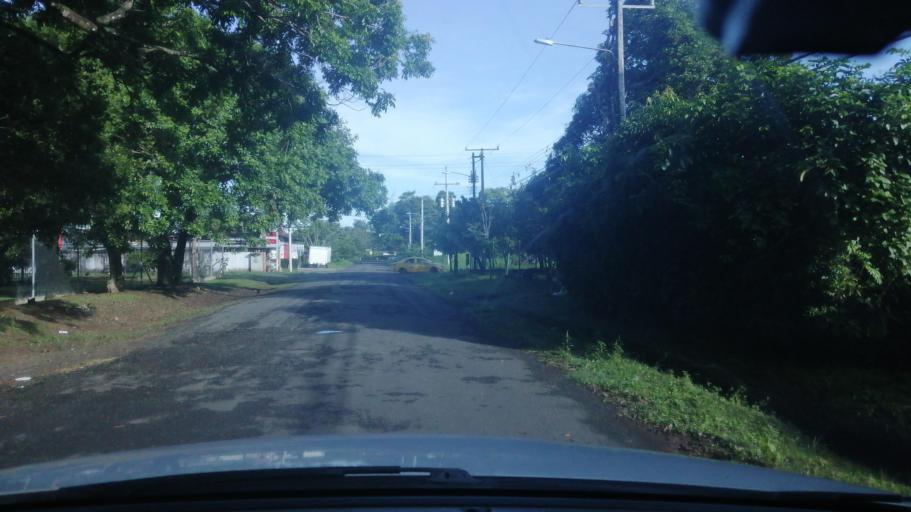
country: PA
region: Chiriqui
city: David
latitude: 8.4434
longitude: -82.4294
